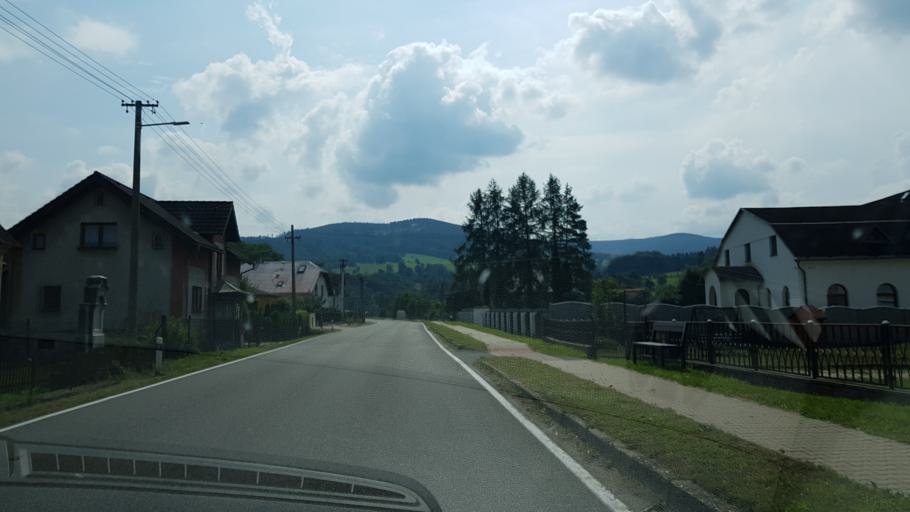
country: CZ
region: Olomoucky
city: Pisecna
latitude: 50.2756
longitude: 17.2796
